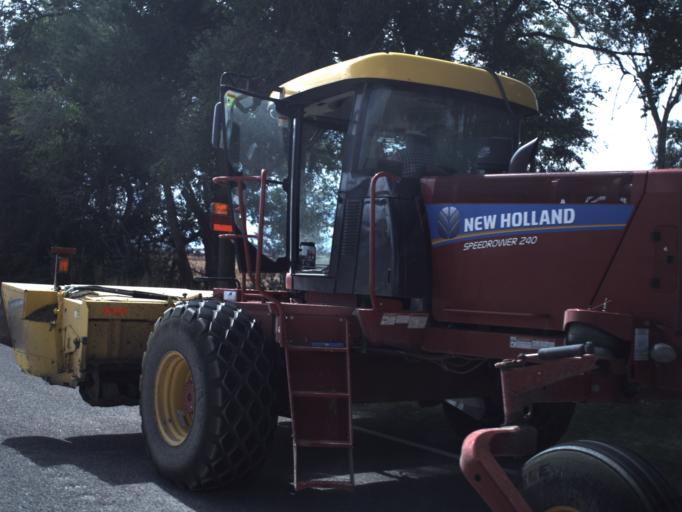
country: US
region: Utah
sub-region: Millard County
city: Fillmore
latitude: 39.0469
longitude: -112.4098
